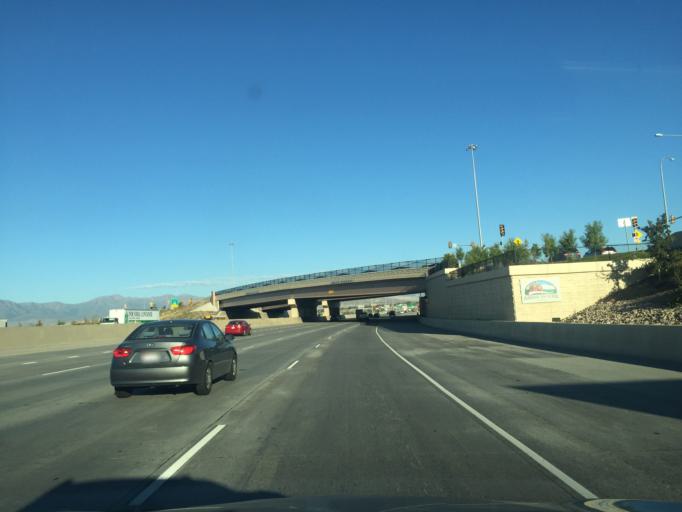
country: US
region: Utah
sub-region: Utah County
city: American Fork
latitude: 40.3760
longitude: -111.8167
